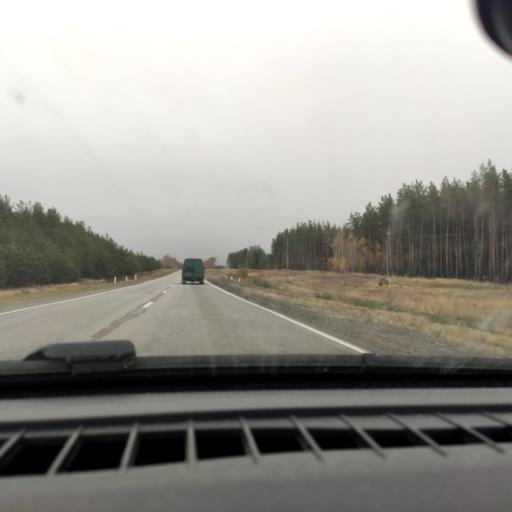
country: RU
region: Voronezj
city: Uryv-Pokrovka
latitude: 51.0547
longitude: 38.9879
